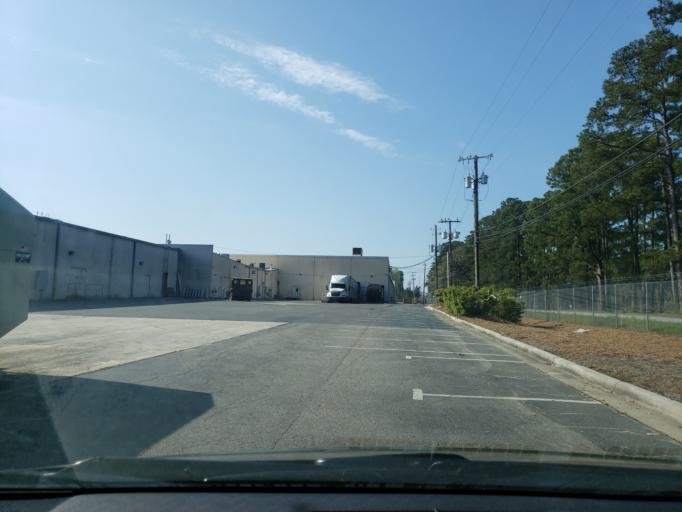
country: US
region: Georgia
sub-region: Chatham County
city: Montgomery
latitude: 32.0046
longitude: -81.1252
